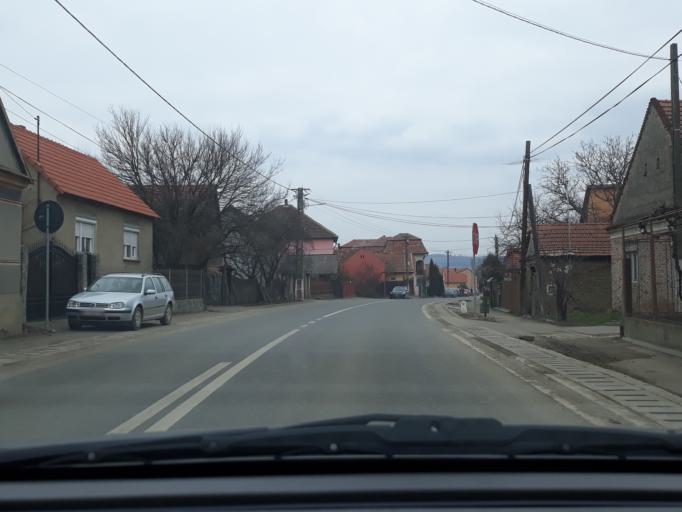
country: RO
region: Salaj
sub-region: Comuna Nusfalau
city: Nusfalau
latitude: 47.1935
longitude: 22.7011
